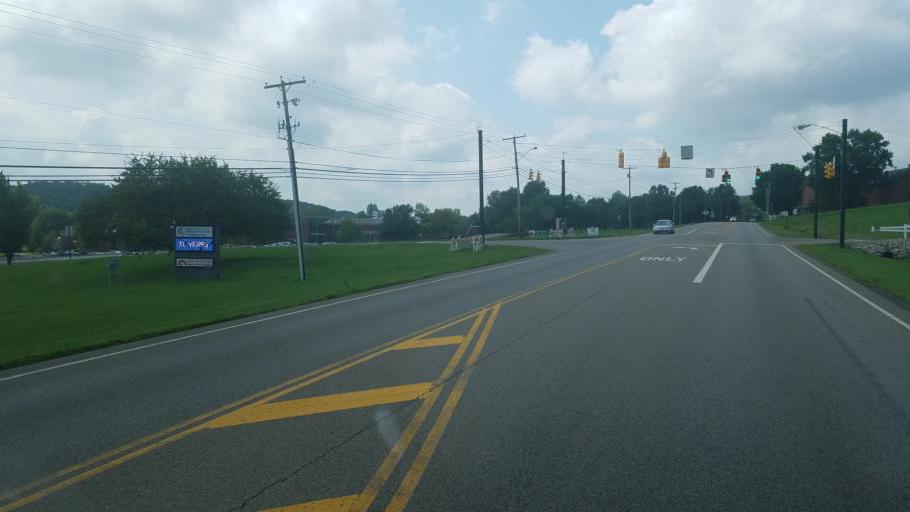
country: US
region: Ohio
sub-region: Fairfield County
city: Lancaster
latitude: 39.7415
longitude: -82.5872
